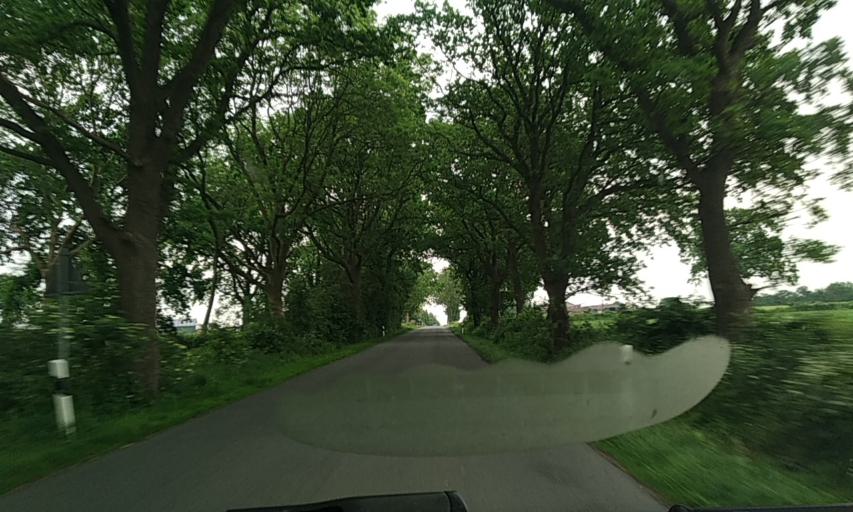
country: DE
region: Schleswig-Holstein
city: Meggerdorf
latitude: 54.3450
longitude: 9.4006
